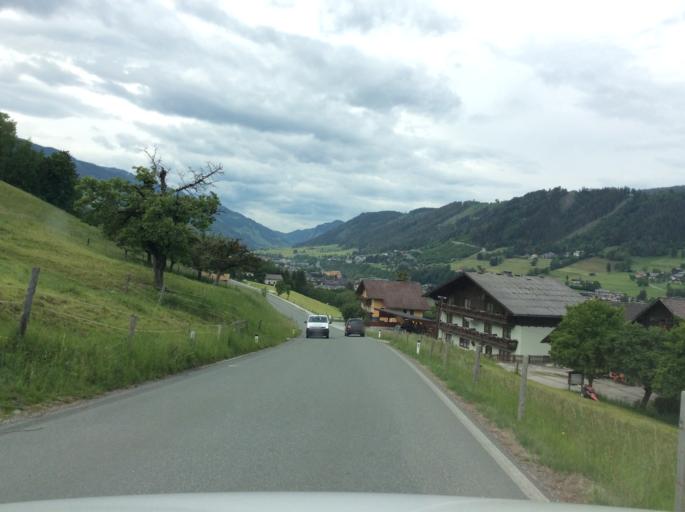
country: AT
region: Styria
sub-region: Politischer Bezirk Liezen
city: Schladming
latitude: 47.3991
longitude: 13.7146
